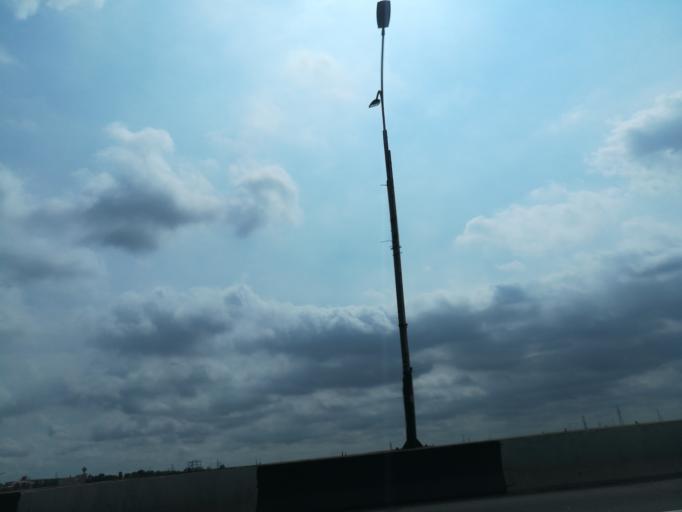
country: NG
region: Lagos
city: Somolu
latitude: 6.5260
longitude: 3.4037
